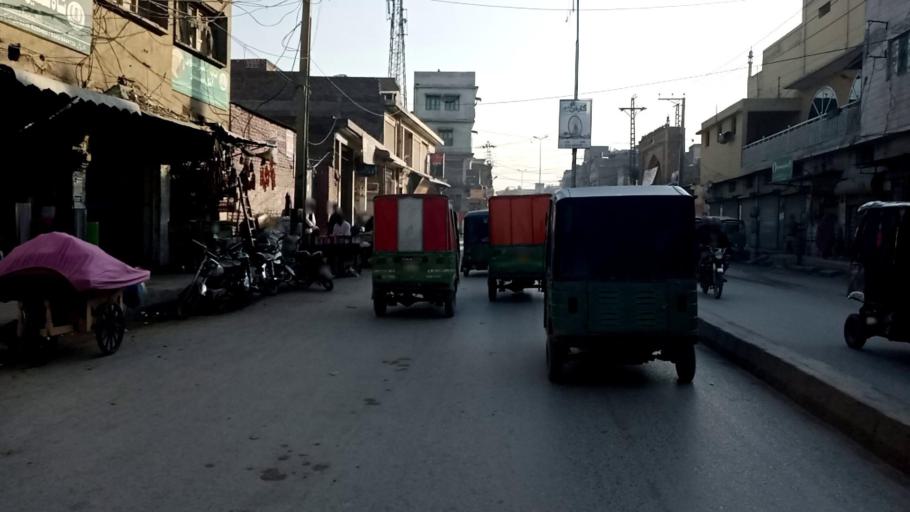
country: PK
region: Khyber Pakhtunkhwa
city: Peshawar
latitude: 34.0069
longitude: 71.5846
